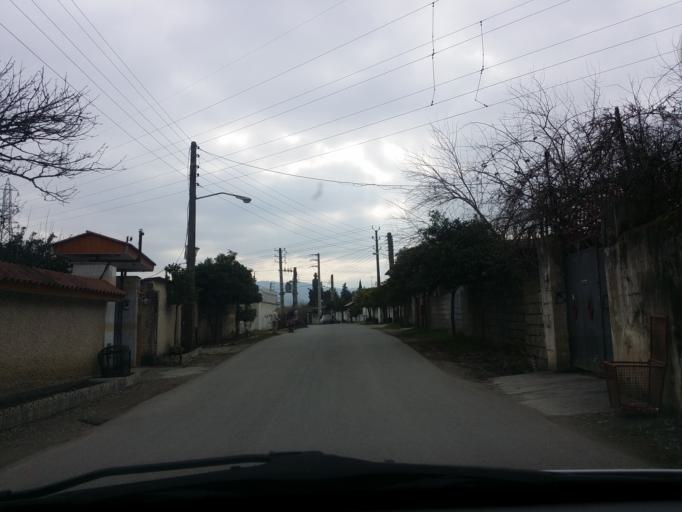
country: IR
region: Mazandaran
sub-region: Nowshahr
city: Nowshahr
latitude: 36.6529
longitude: 51.4759
